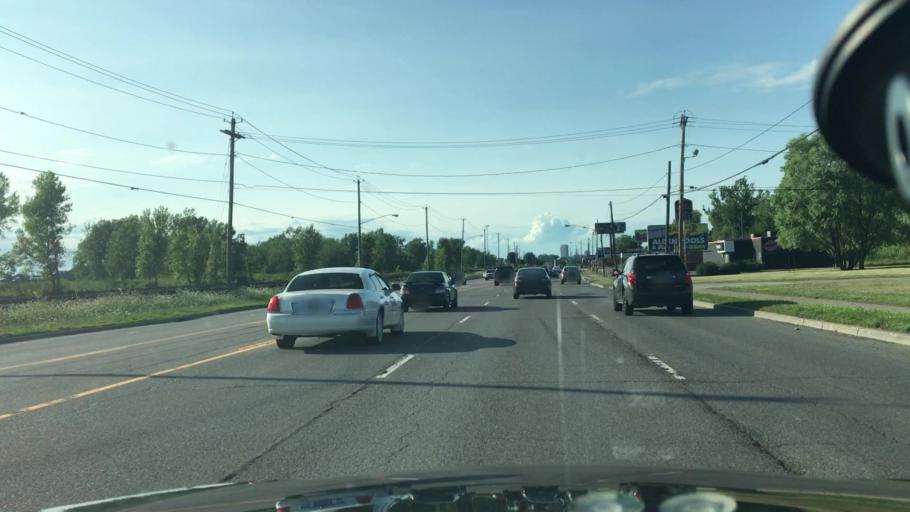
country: US
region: New York
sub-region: Erie County
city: Lackawanna
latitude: 42.8169
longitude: -78.8465
